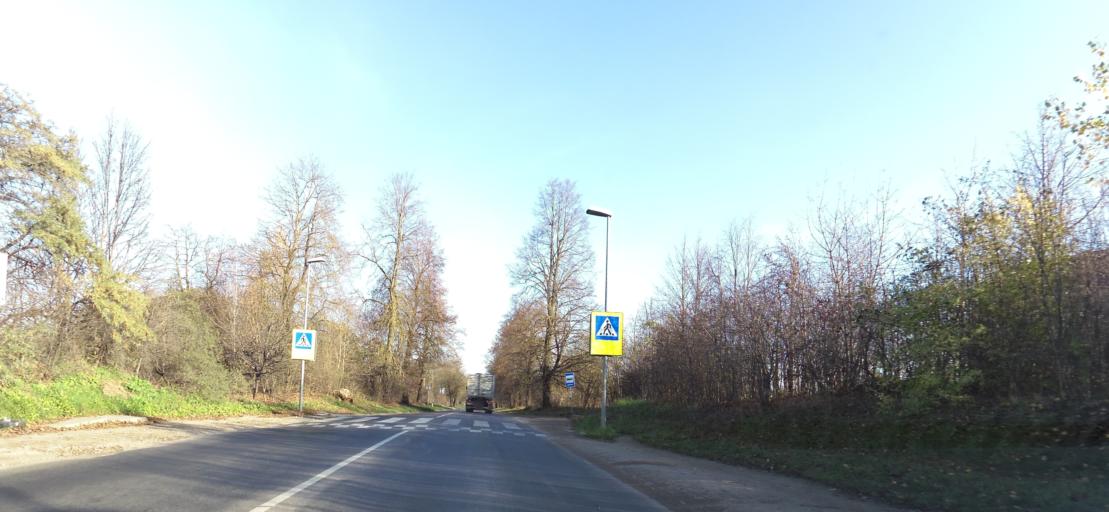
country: LT
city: Grigiskes
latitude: 54.6471
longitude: 25.1278
